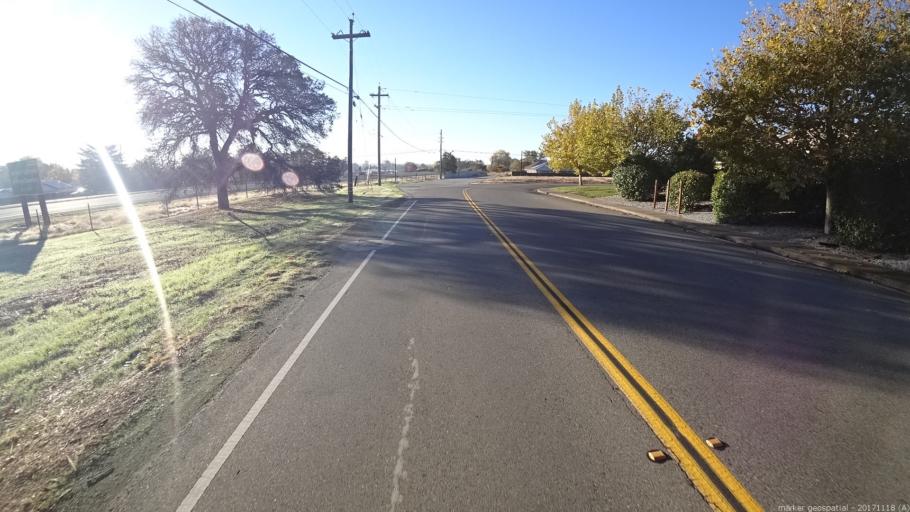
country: US
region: California
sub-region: Shasta County
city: Cottonwood
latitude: 40.3982
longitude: -122.2840
